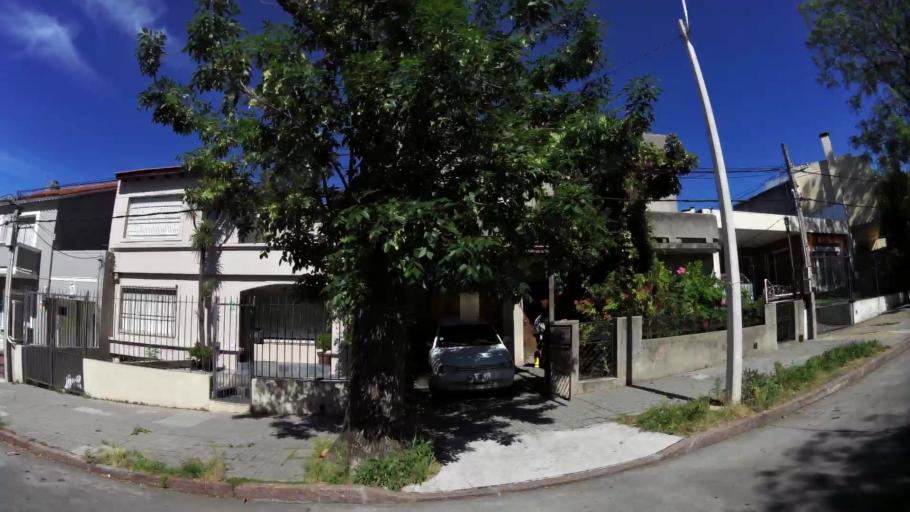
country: UY
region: Montevideo
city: Montevideo
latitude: -34.8979
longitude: -56.1508
